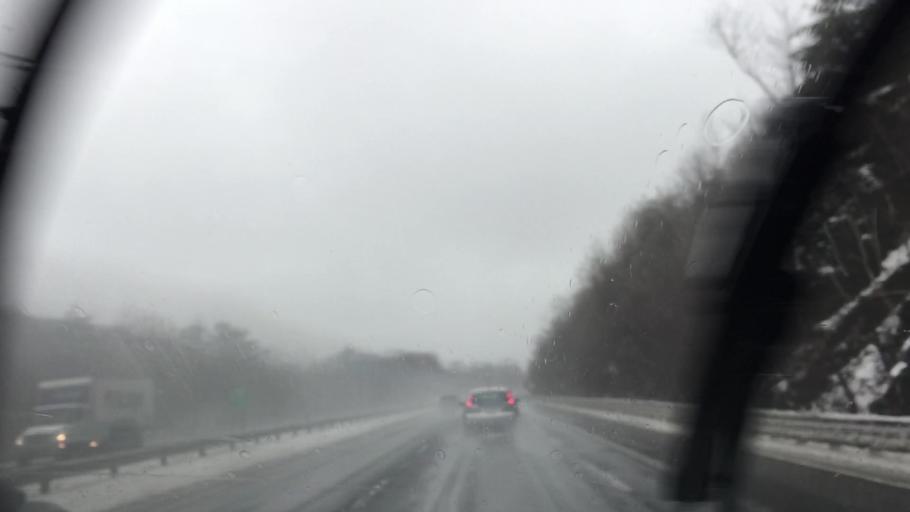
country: US
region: Massachusetts
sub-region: Hampden County
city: Granville
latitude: 42.1710
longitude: -72.8872
